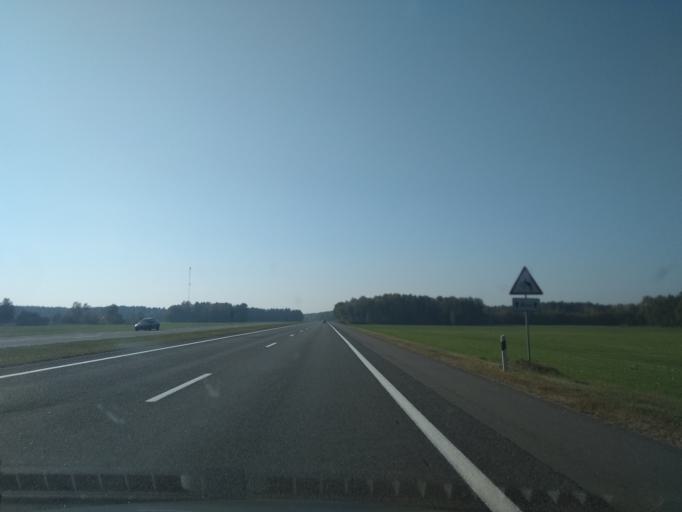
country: BY
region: Brest
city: Antopal'
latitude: 52.3570
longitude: 24.6989
